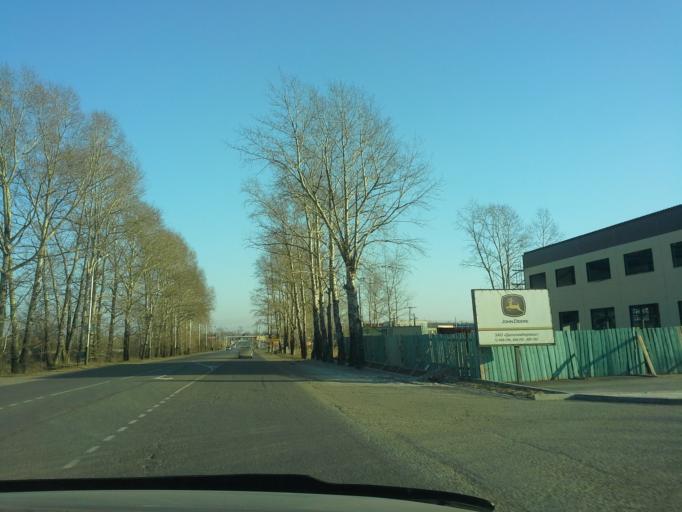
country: RU
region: Khabarovsk Krai
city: Topolevo
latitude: 48.4759
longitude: 135.1668
